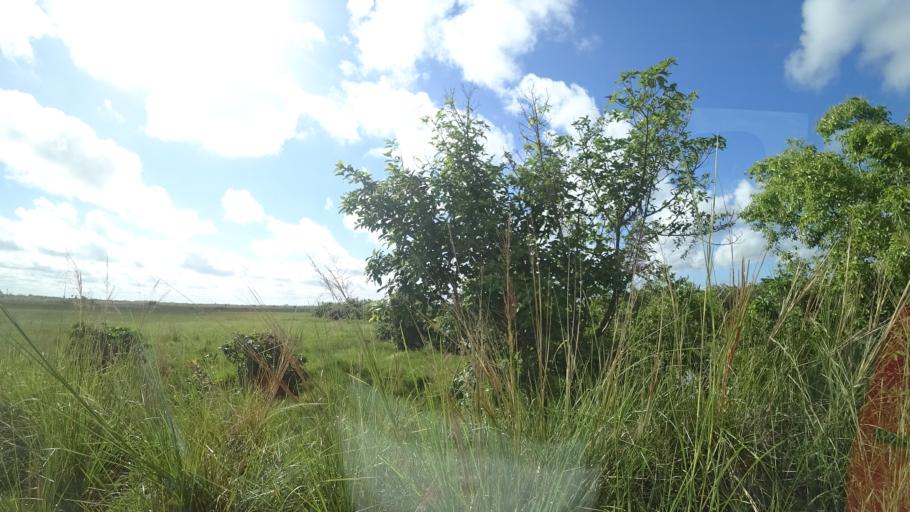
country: MZ
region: Sofala
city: Beira
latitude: -19.6292
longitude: 35.0601
